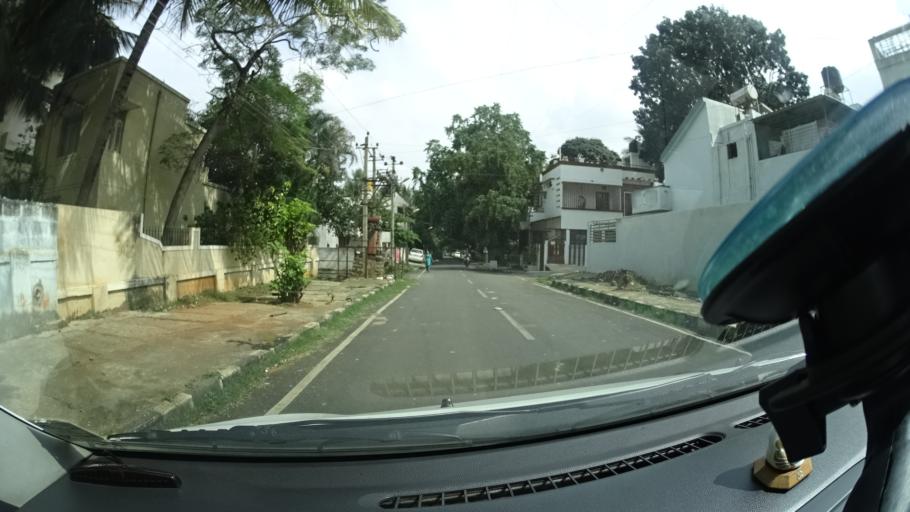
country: IN
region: Karnataka
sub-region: Bangalore Urban
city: Yelahanka
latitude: 13.1026
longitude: 77.5698
